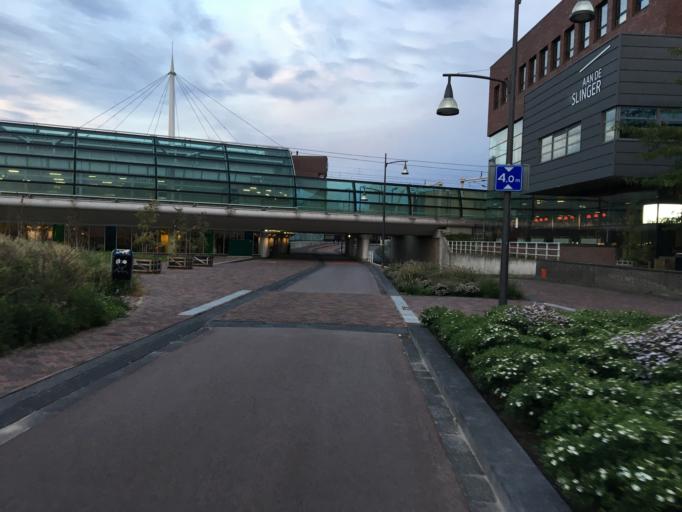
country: NL
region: Utrecht
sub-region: Gemeente Houten
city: Houten
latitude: 52.0334
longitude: 5.1675
